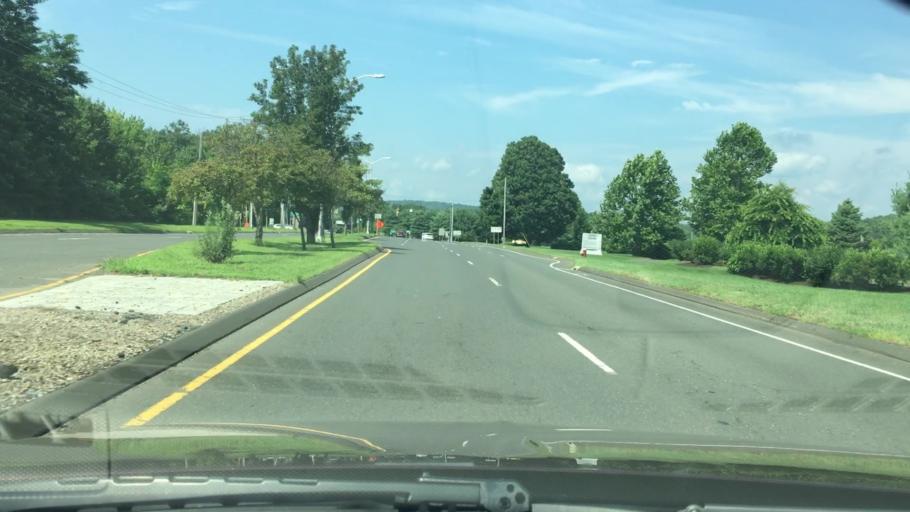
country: US
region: Connecticut
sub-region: Hartford County
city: Tariffville
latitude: 41.8761
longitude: -72.7279
